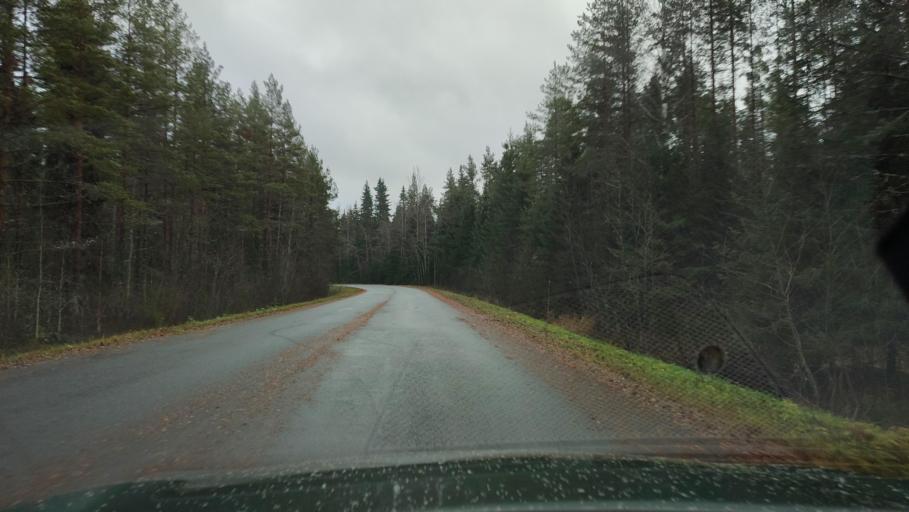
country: FI
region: Southern Ostrobothnia
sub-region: Suupohja
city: Teuva
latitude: 62.4586
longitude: 21.5819
